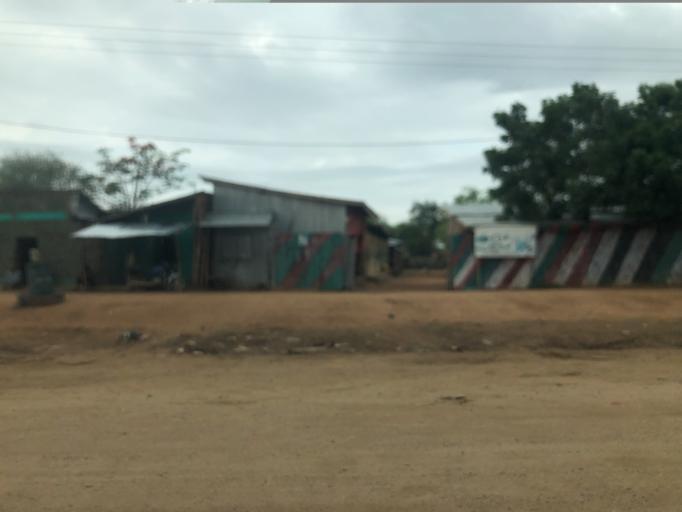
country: ET
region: Southern Nations, Nationalities, and People's Region
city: Turmi
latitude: 4.9702
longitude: 36.4869
